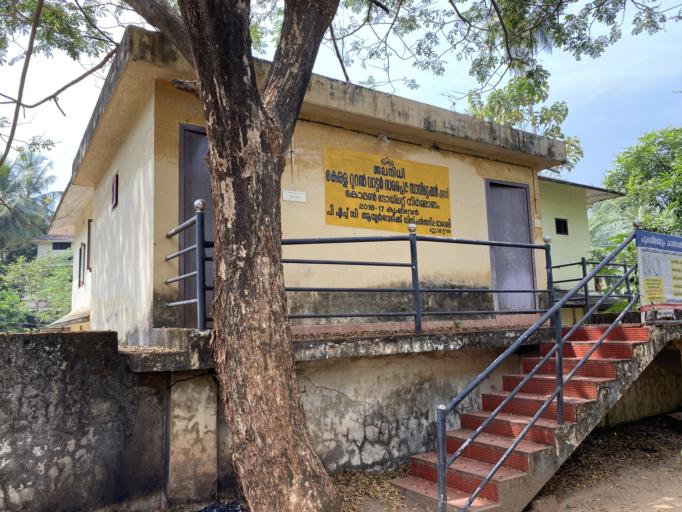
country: IN
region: Kerala
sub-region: Malappuram
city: Malappuram
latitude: 11.0628
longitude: 76.0177
